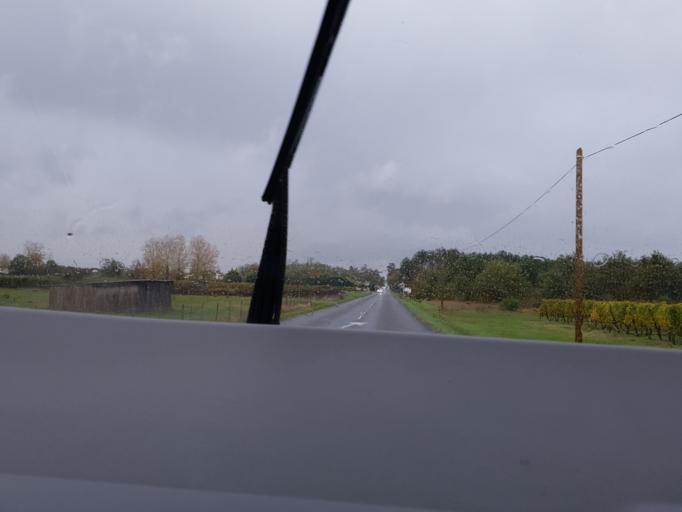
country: FR
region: Aquitaine
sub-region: Departement de la Gironde
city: Marcillac
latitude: 45.2419
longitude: -0.5381
